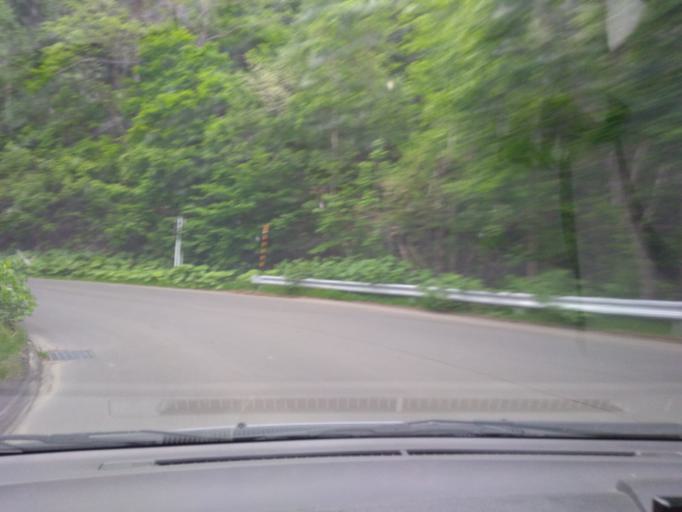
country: JP
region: Hokkaido
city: Shimo-furano
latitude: 43.1408
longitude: 142.4630
